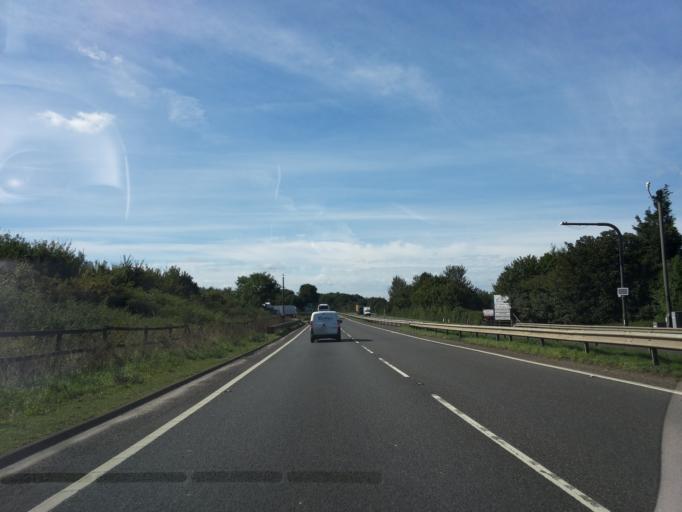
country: GB
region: England
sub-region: Kent
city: Boxley
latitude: 51.2998
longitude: 0.5922
